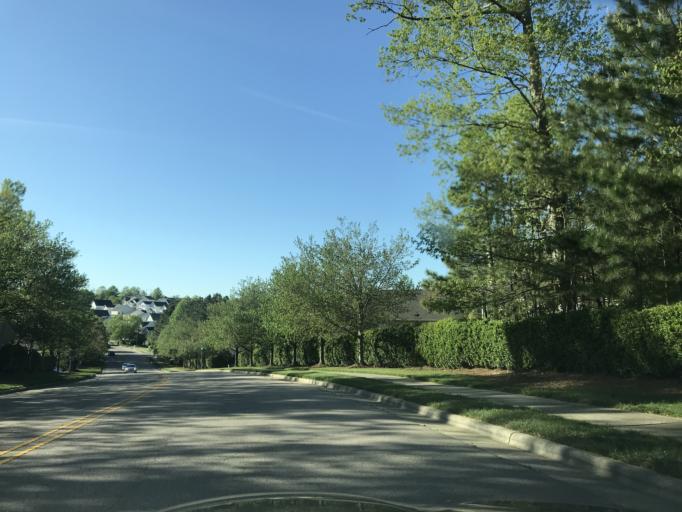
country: US
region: North Carolina
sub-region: Wake County
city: Knightdale
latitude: 35.8374
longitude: -78.5619
